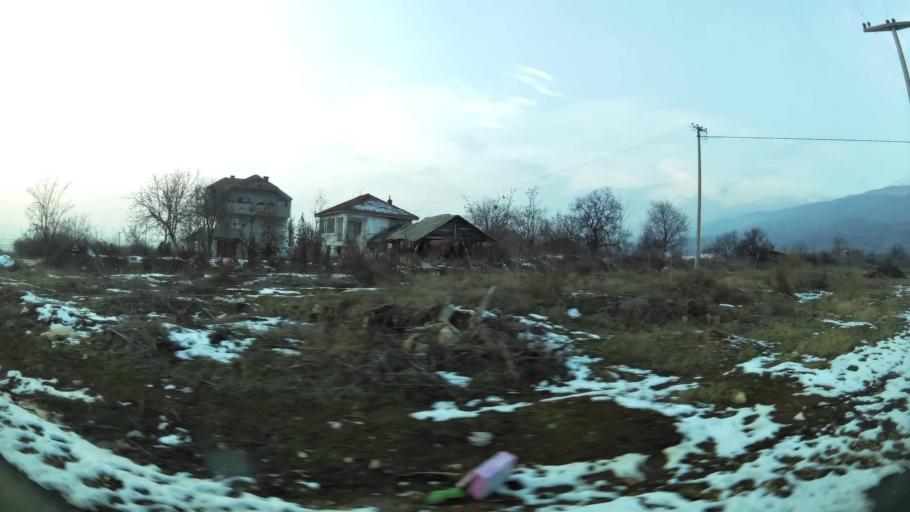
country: MK
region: Aracinovo
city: Arachinovo
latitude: 42.0300
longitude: 21.5473
